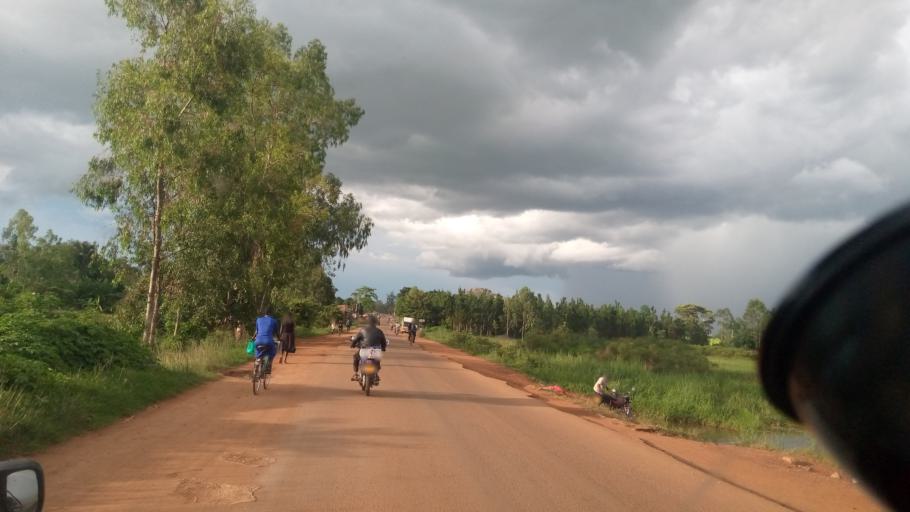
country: UG
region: Northern Region
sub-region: Lira District
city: Lira
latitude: 2.2709
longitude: 32.9154
